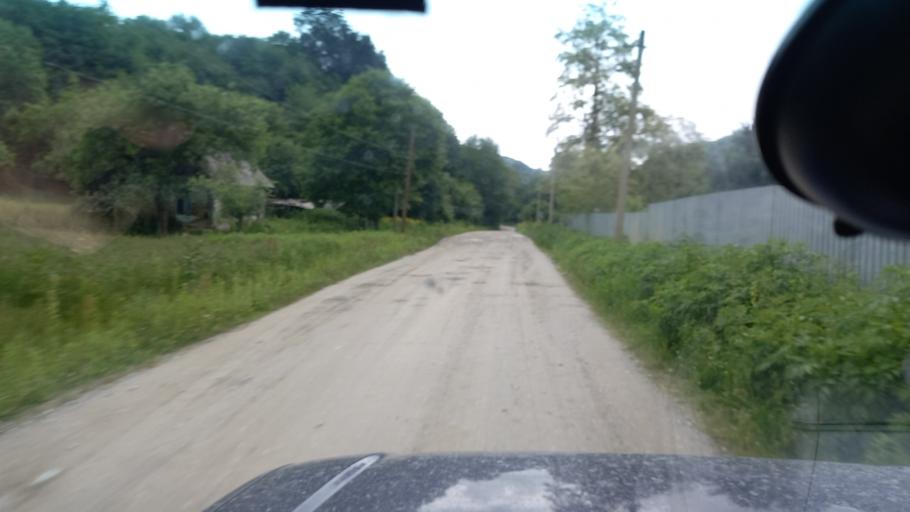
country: RU
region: Krasnodarskiy
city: Psebay
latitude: 44.0232
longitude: 40.7313
